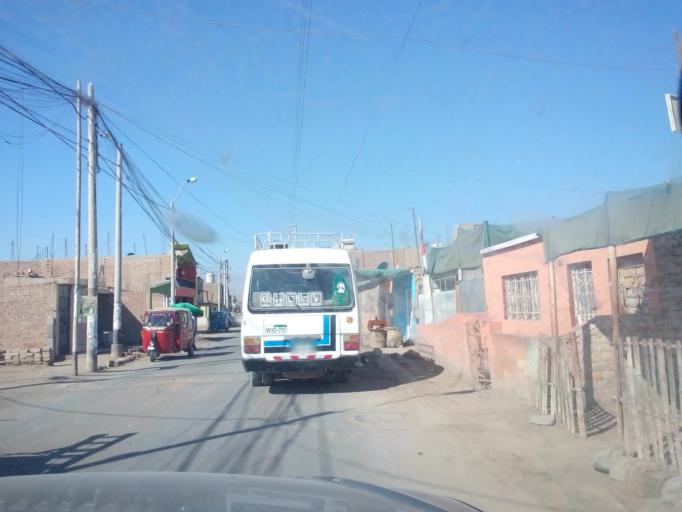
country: PE
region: Ica
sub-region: Provincia de Ica
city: Ica
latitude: -14.0741
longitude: -75.7524
